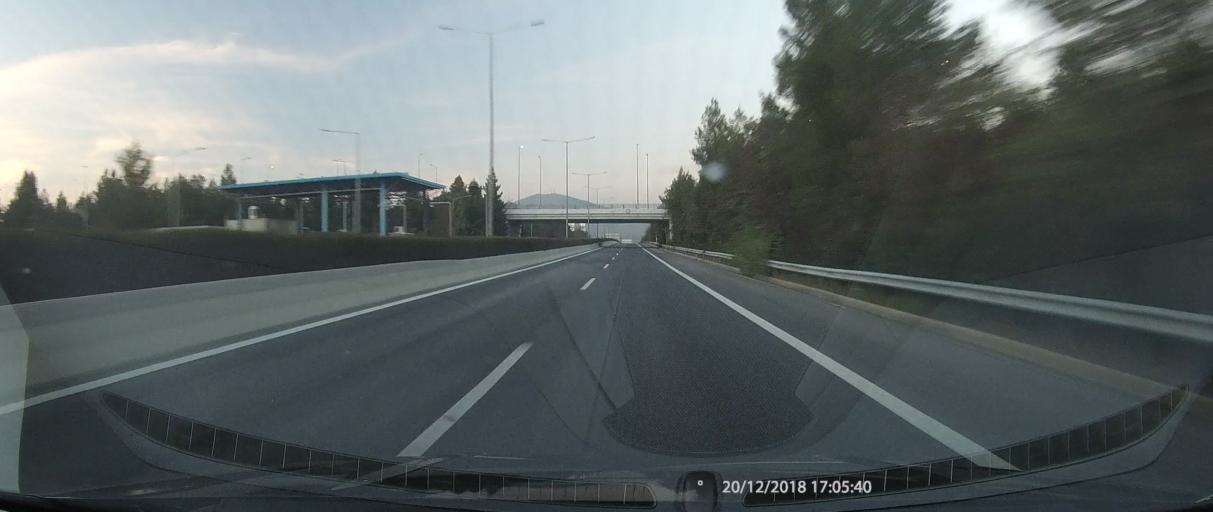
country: GR
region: Thessaly
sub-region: Nomos Larisis
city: Makrychori
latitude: 39.7442
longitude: 22.4758
